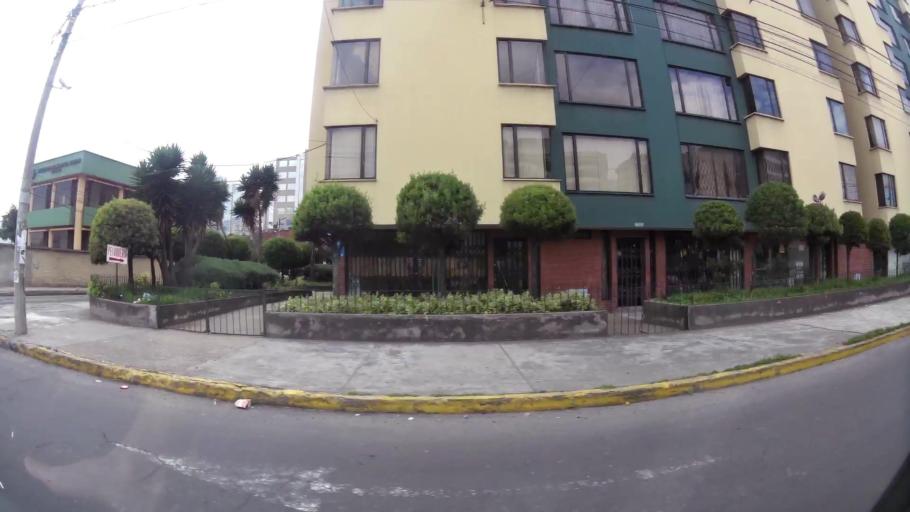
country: EC
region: Pichincha
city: Quito
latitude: -0.1701
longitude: -78.4865
